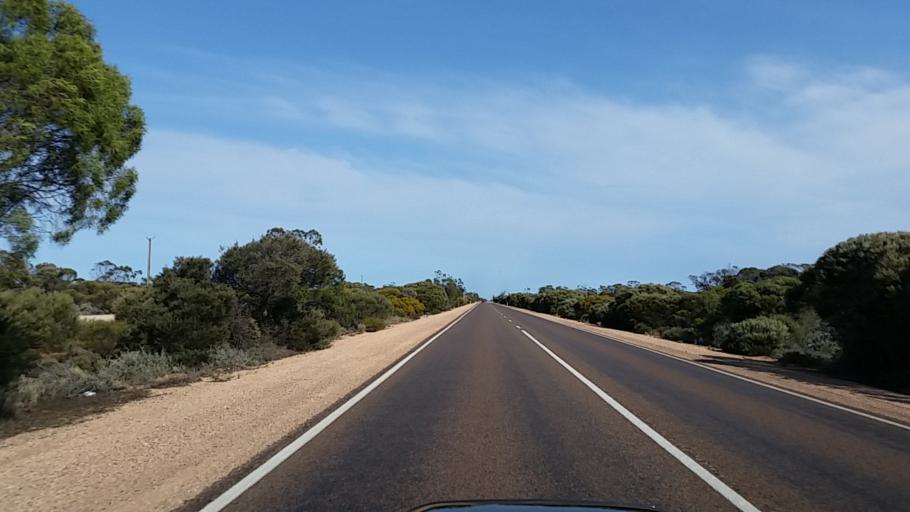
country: AU
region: South Australia
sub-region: Whyalla
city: Whyalla
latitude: -32.9418
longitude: 137.5725
